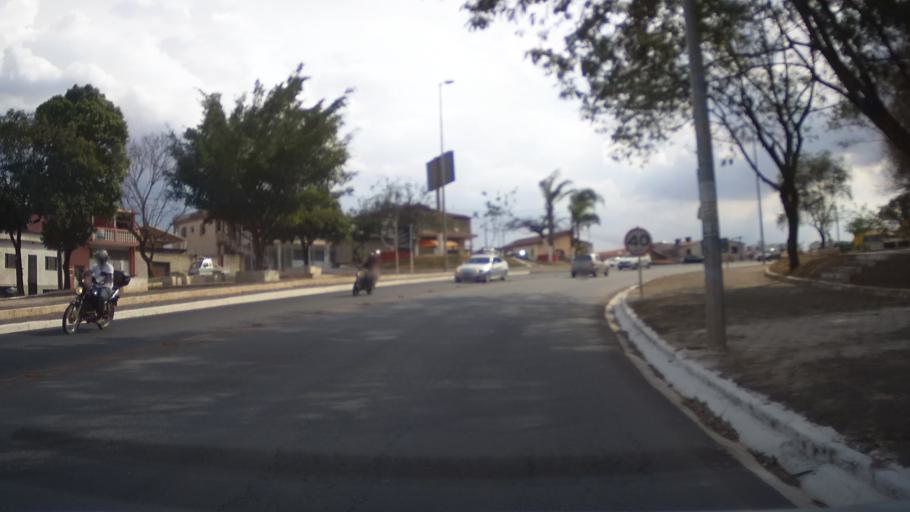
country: BR
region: Minas Gerais
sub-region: Belo Horizonte
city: Belo Horizonte
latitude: -19.8766
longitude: -43.8979
